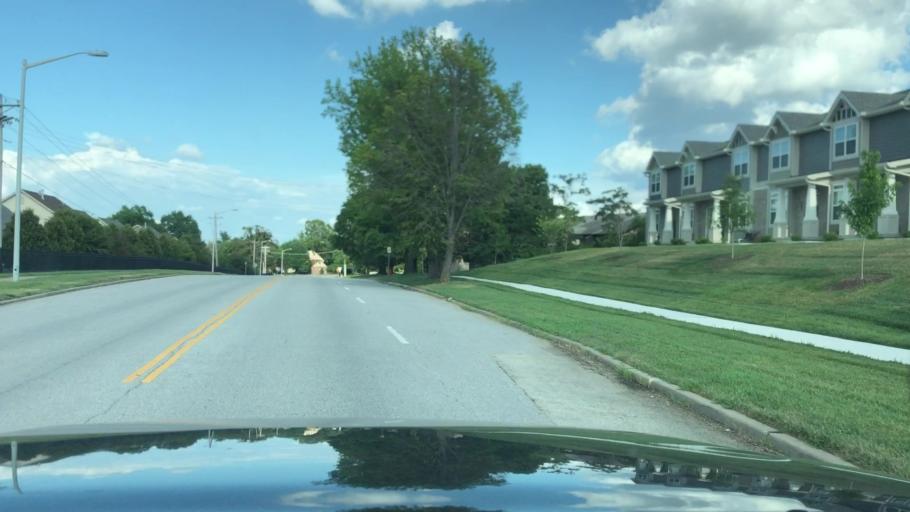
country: US
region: Missouri
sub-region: Saint Charles County
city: Lake Saint Louis
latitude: 38.7959
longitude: -90.8111
